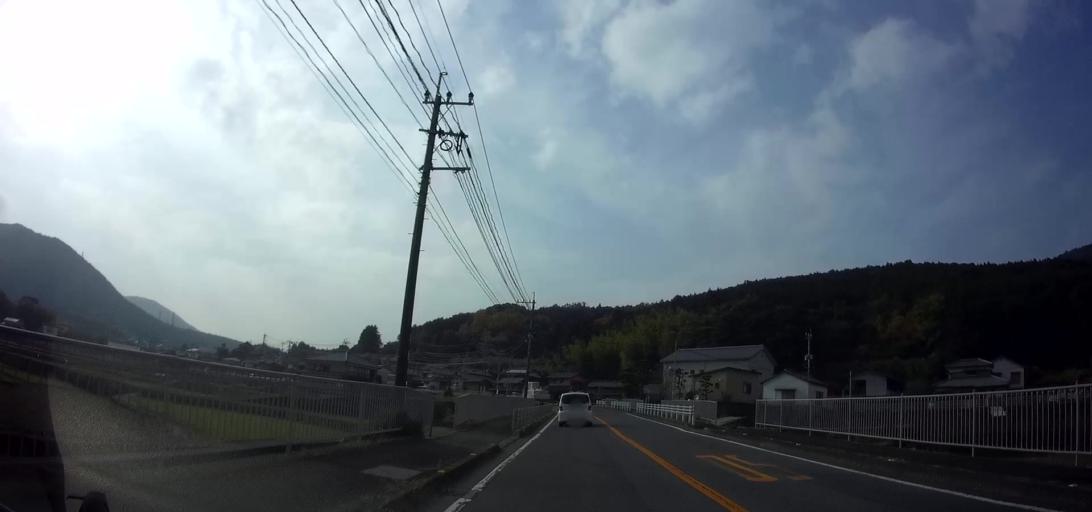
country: JP
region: Nagasaki
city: Shimabara
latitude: 32.7691
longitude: 130.2138
